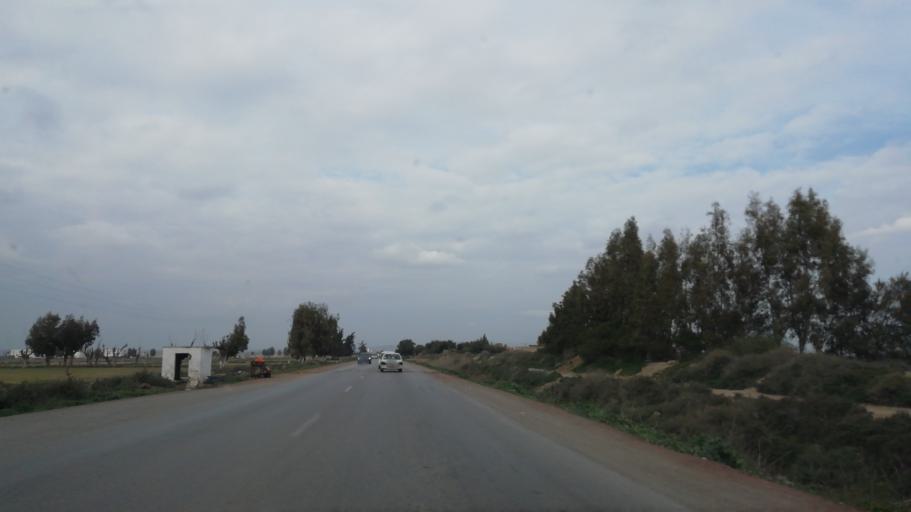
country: DZ
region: Mostaganem
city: Mostaganem
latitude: 35.6856
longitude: 0.0565
